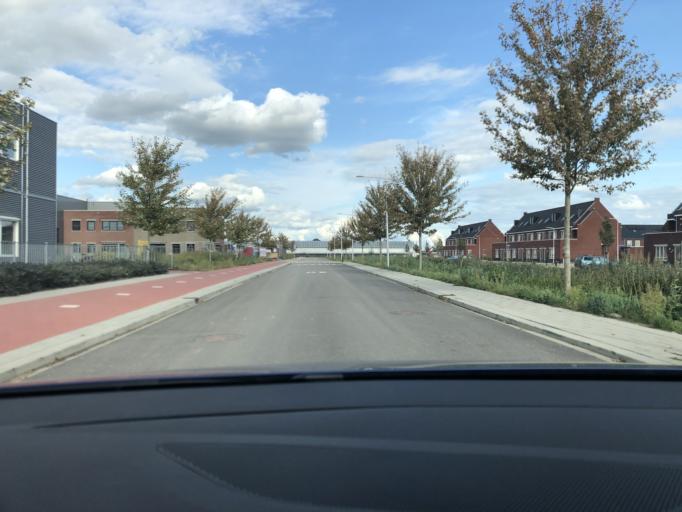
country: NL
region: South Holland
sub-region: Gemeente Lansingerland
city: Bleiswijk
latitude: 52.0068
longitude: 4.5915
